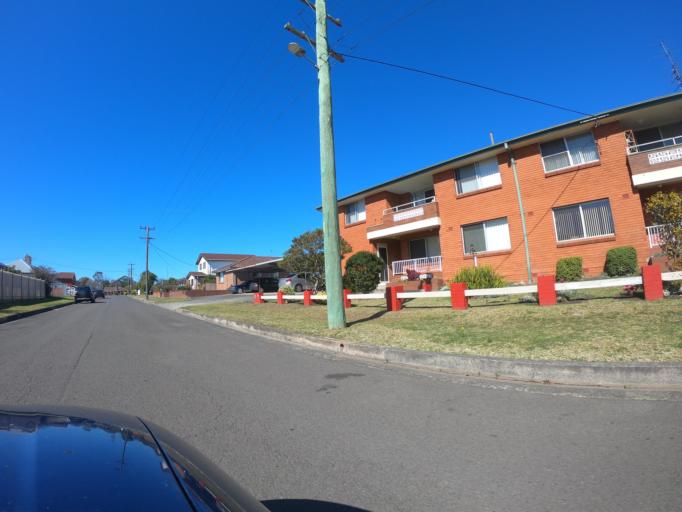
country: AU
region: New South Wales
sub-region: Wollongong
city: Koonawarra
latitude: -34.4818
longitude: 150.8057
